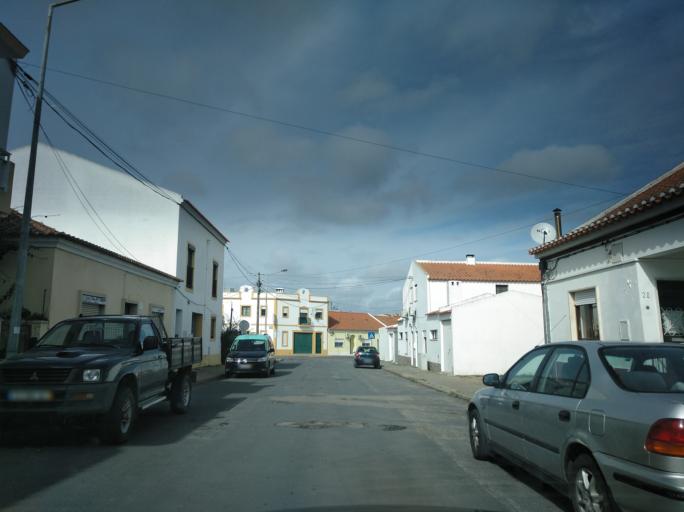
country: PT
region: Setubal
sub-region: Grandola
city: Grandola
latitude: 38.1767
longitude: -8.5610
